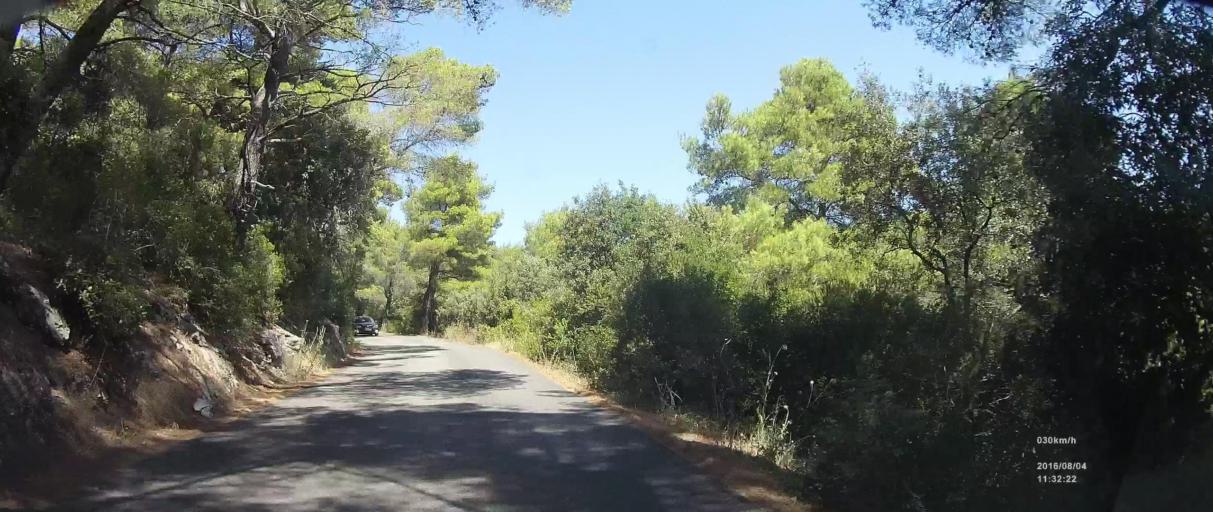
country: HR
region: Dubrovacko-Neretvanska
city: Blato
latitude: 42.7880
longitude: 17.3748
